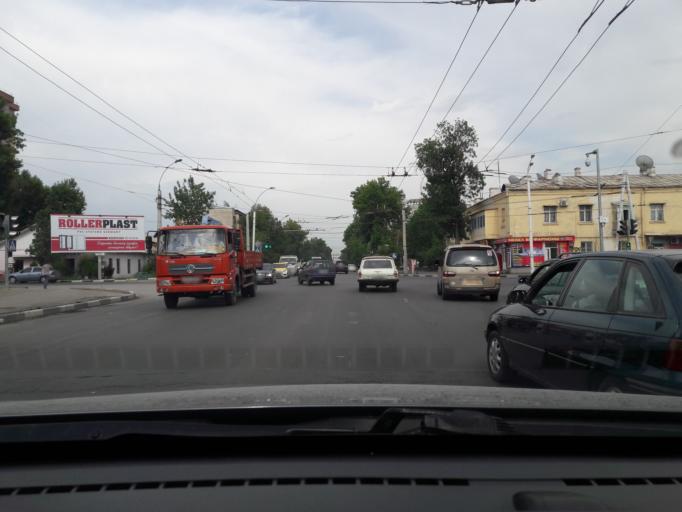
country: TJ
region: Dushanbe
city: Dushanbe
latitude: 38.5461
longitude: 68.7548
